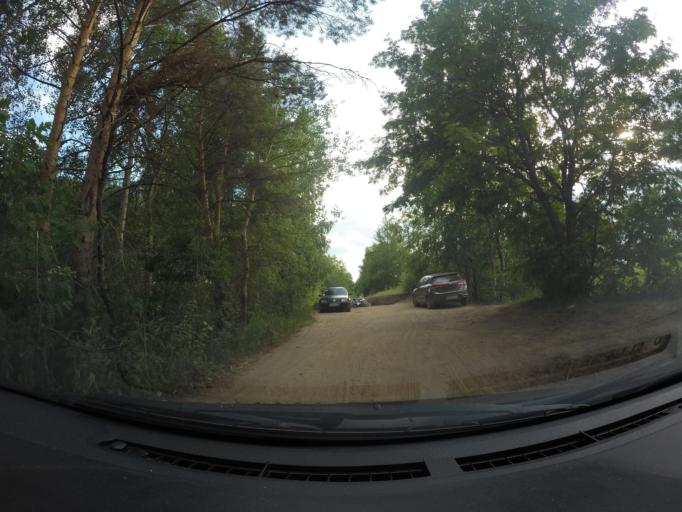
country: RU
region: Moskovskaya
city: Krasnyy Tkach
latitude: 55.4165
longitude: 39.2289
